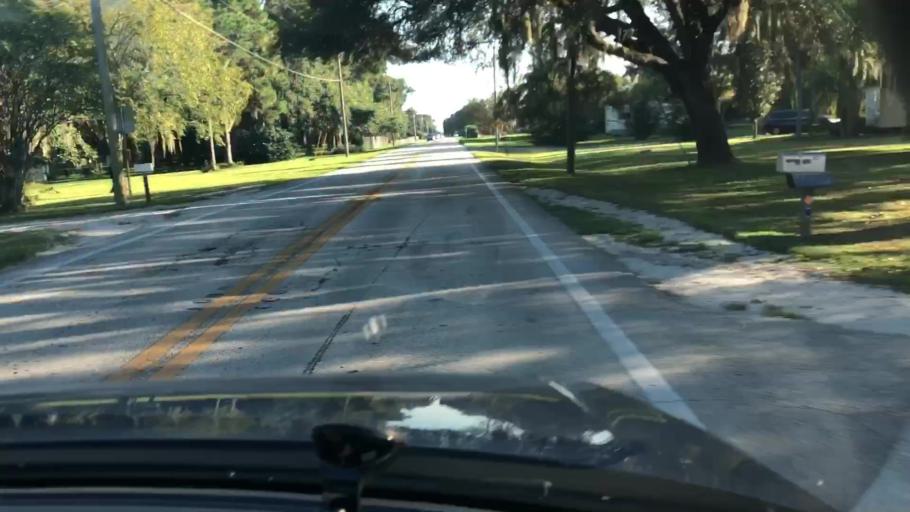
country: US
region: Florida
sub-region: Polk County
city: Gibsonia
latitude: 28.1412
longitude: -81.9384
